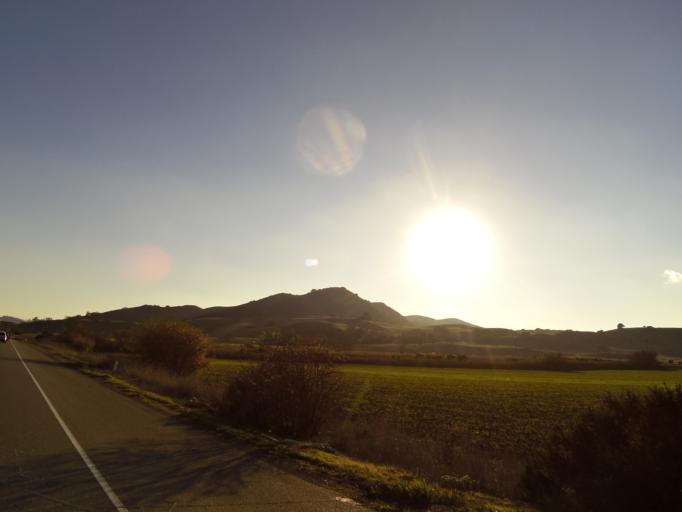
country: US
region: California
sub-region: Santa Clara County
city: Gilroy
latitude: 36.9449
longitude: -121.5530
